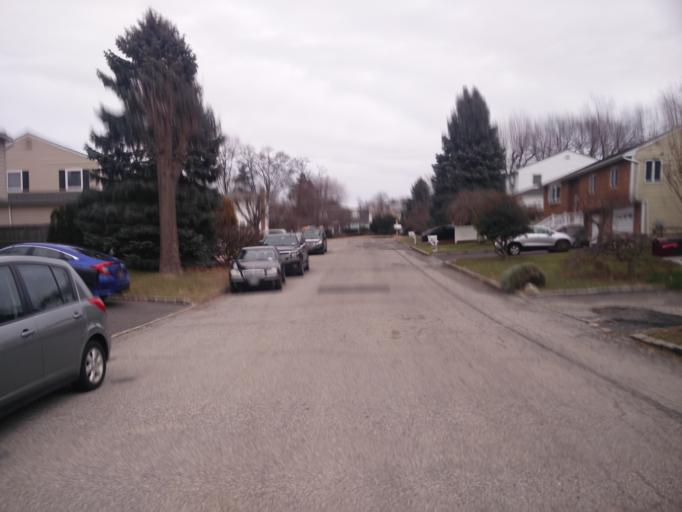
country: US
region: New York
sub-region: Nassau County
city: Glen Cove
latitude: 40.8747
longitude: -73.6289
